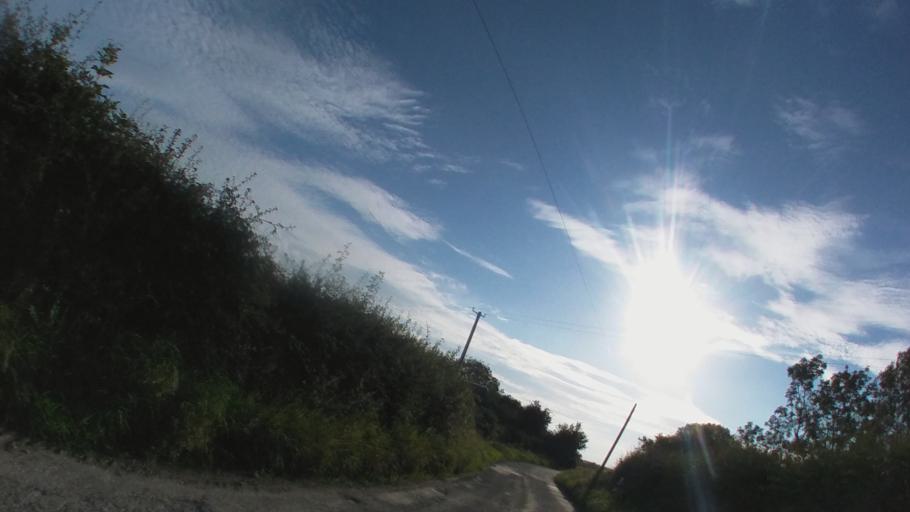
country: IE
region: Leinster
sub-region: Kilkenny
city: Kilkenny
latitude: 52.6950
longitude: -7.1920
